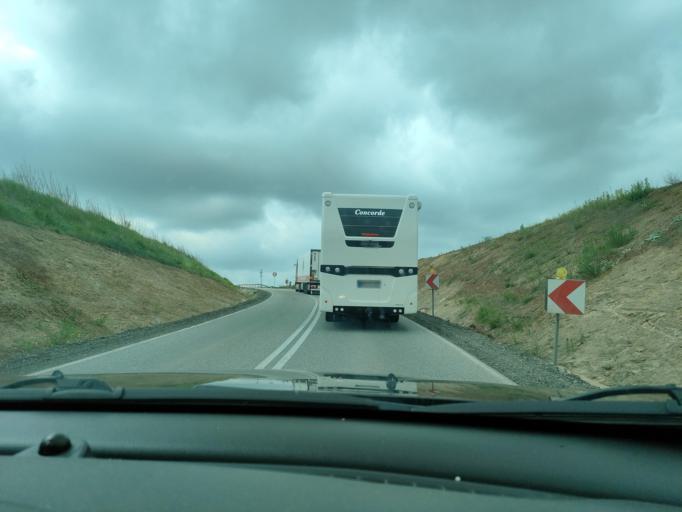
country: PL
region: Kujawsko-Pomorskie
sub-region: Powiat swiecki
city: Bukowiec
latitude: 53.3531
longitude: 18.3049
